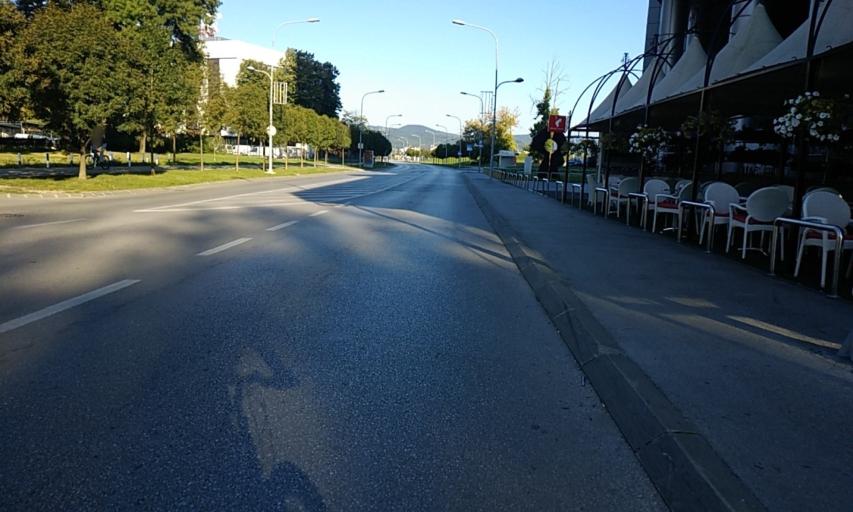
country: BA
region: Republika Srpska
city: Banja Luka
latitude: 44.7784
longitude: 17.1986
